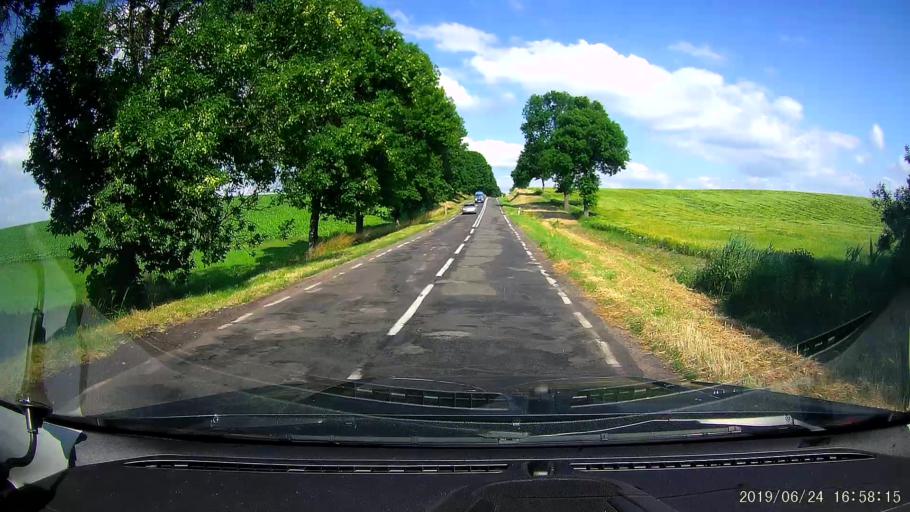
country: PL
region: Lublin Voivodeship
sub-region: Powiat tomaszowski
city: Telatyn
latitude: 50.5254
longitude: 23.8764
